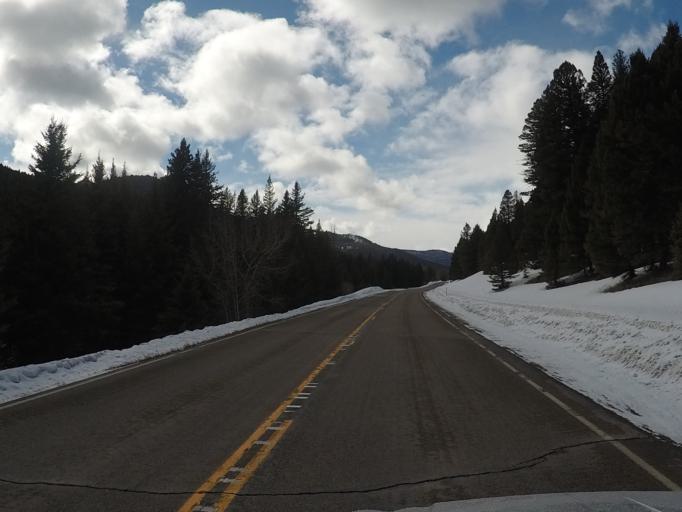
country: US
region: Montana
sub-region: Meagher County
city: White Sulphur Springs
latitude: 46.7601
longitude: -110.7316
